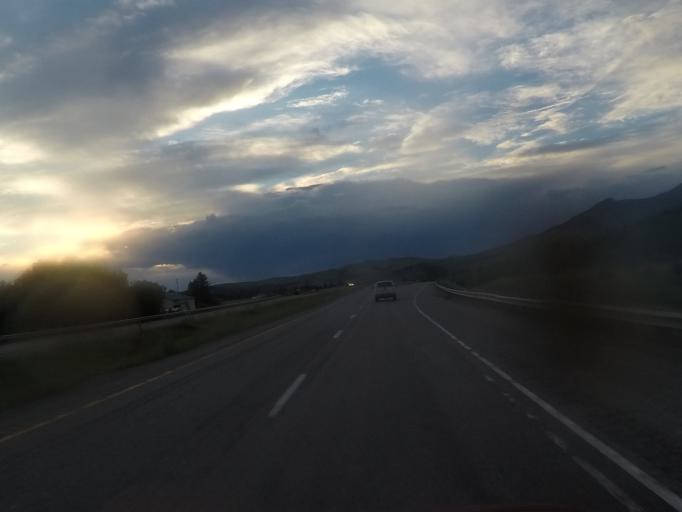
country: US
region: Montana
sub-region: Gallatin County
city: Bozeman
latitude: 45.6507
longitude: -110.9419
